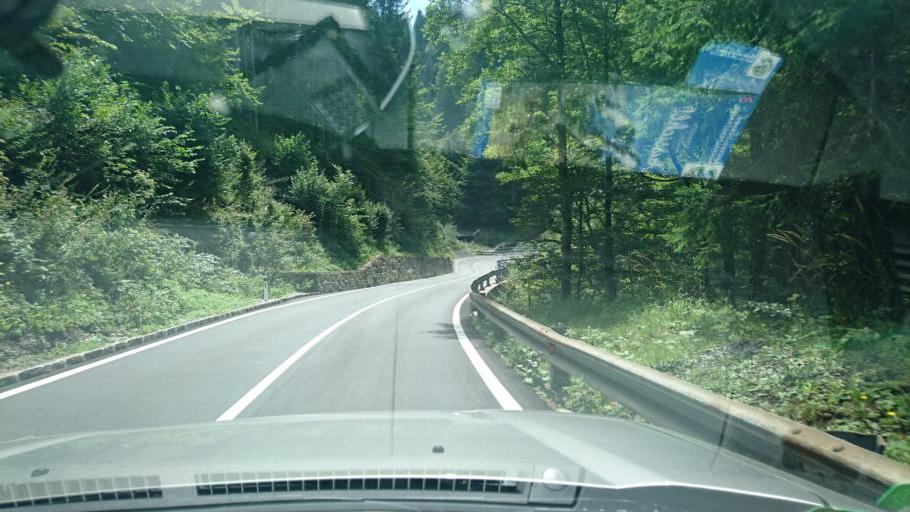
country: AT
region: Carinthia
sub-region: Politischer Bezirk Villach Land
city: Arnoldstein
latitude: 46.5276
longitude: 13.7519
